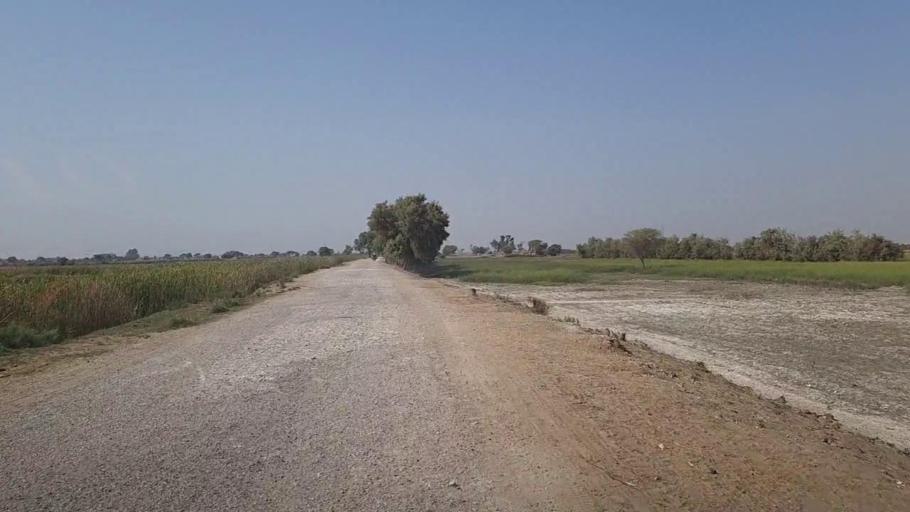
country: PK
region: Sindh
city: Kandhkot
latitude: 28.4026
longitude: 69.2601
